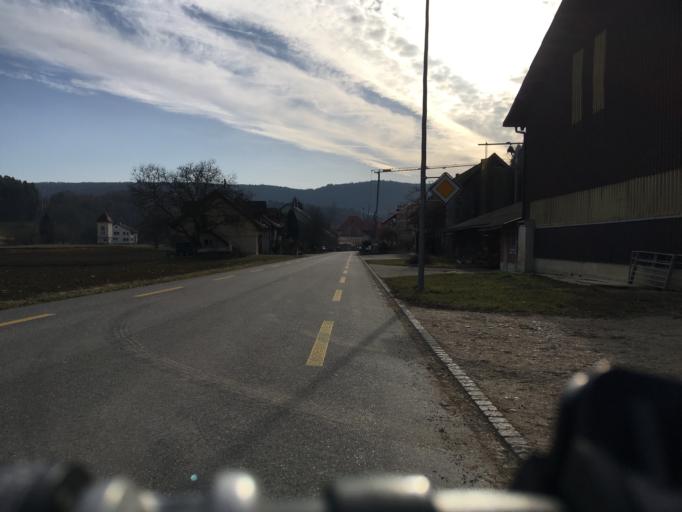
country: DE
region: Baden-Wuerttemberg
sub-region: Freiburg Region
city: Tengen
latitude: 47.7846
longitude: 8.6792
